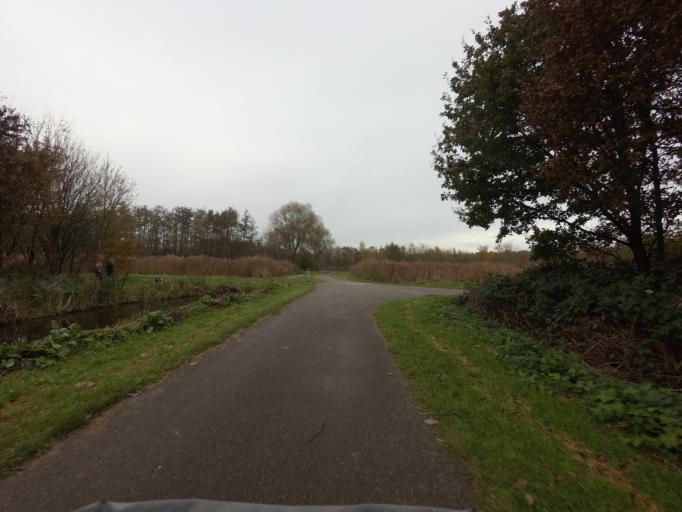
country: NL
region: North Holland
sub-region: Gemeente Amsterdam
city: Driemond
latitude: 52.3254
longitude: 4.9979
